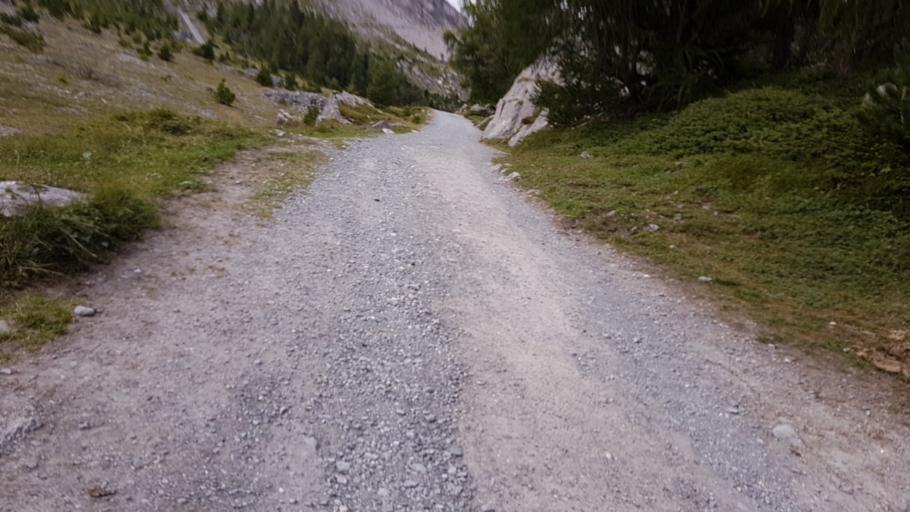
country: CH
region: Bern
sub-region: Frutigen-Niedersimmental District
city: Kandersteg
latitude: 46.4421
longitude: 7.6387
